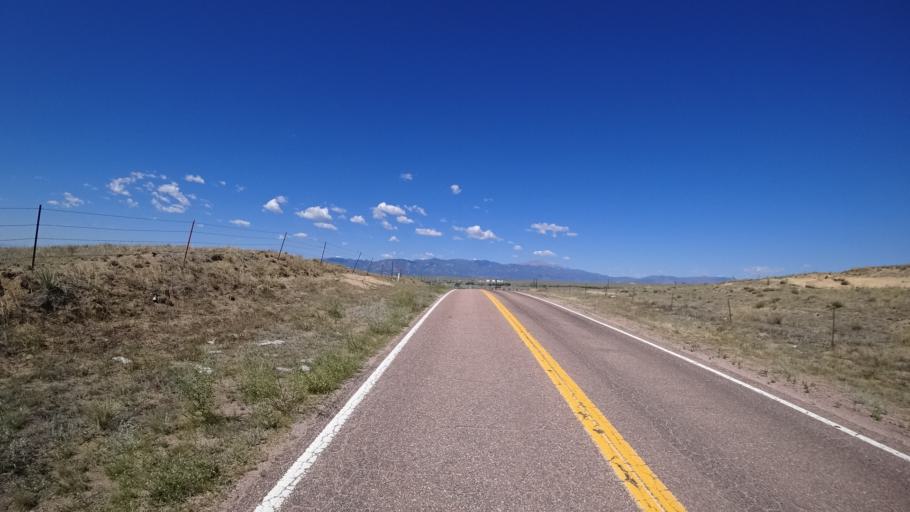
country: US
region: Colorado
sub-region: El Paso County
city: Security-Widefield
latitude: 38.7810
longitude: -104.6213
